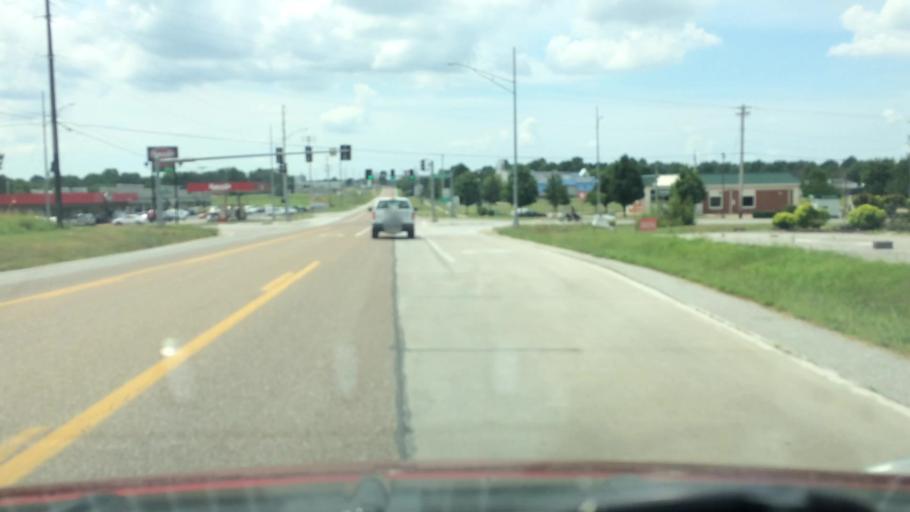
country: US
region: Missouri
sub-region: Greene County
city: Springfield
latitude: 37.2632
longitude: -93.2649
